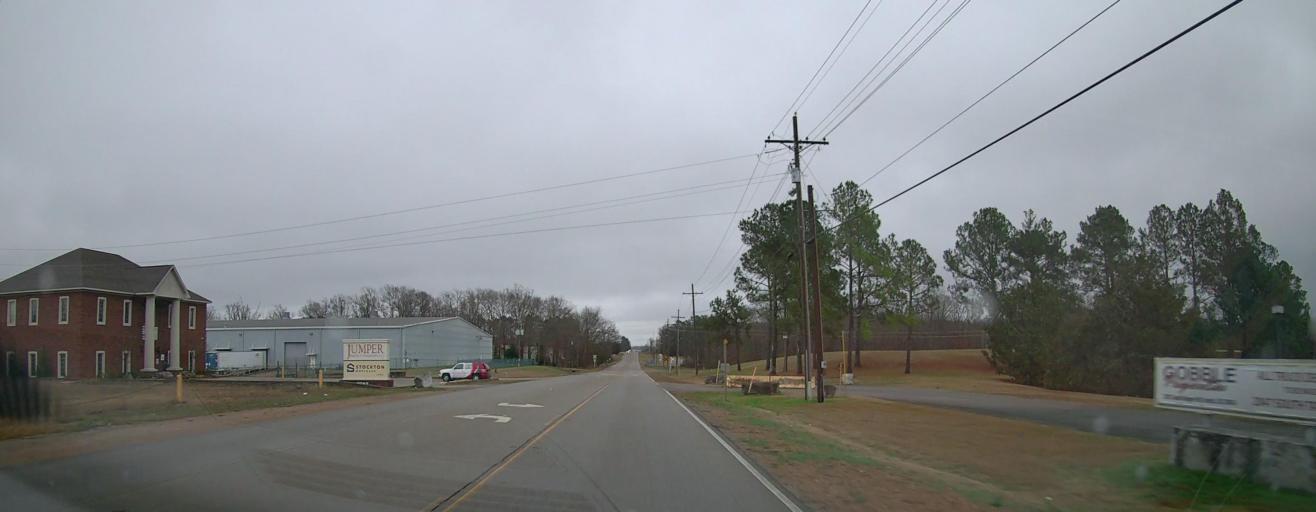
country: US
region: Mississippi
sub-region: Alcorn County
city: Corinth
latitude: 34.9089
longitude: -88.5390
